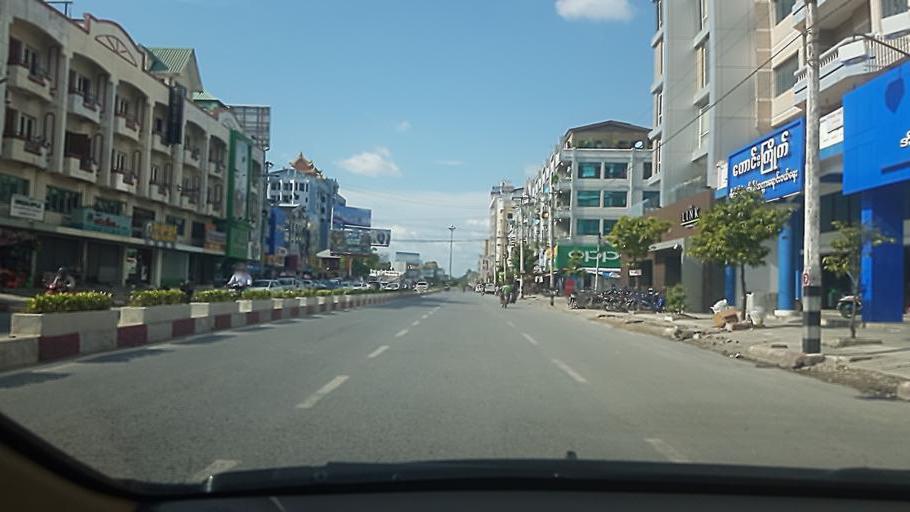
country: MM
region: Mandalay
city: Mandalay
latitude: 21.9747
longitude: 96.0869
